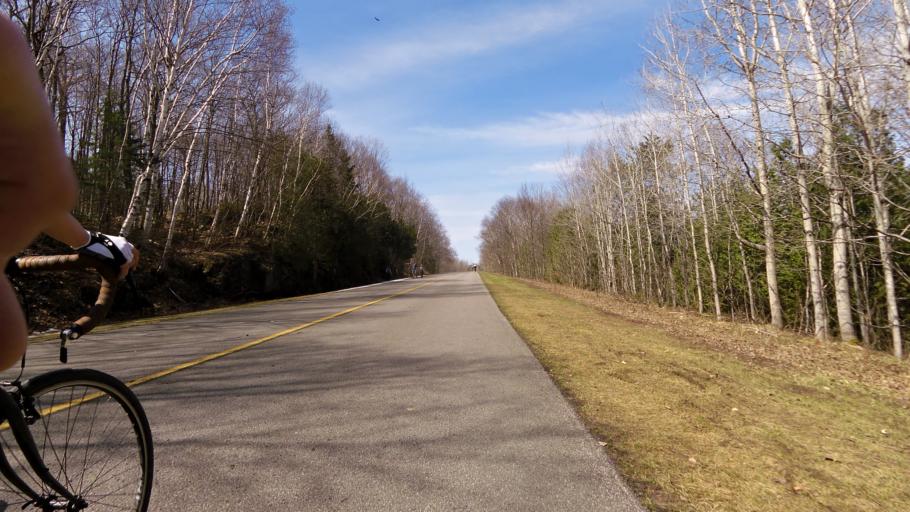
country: CA
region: Quebec
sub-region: Outaouais
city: Gatineau
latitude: 45.4535
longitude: -75.7800
